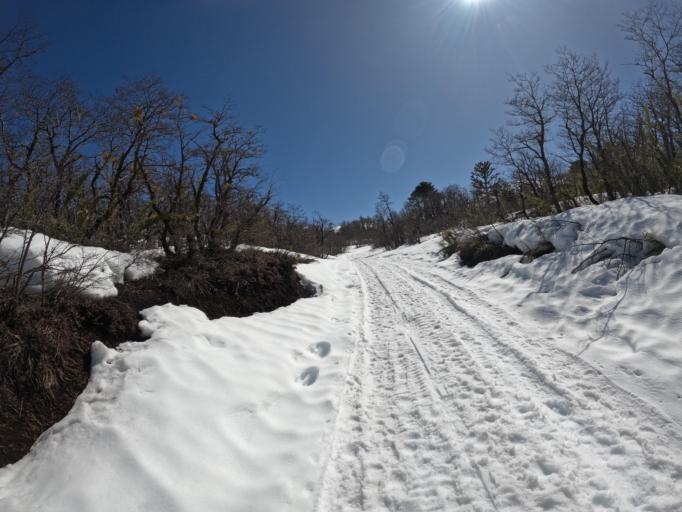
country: CL
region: Araucania
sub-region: Provincia de Cautin
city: Vilcun
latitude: -38.6596
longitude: -71.6185
